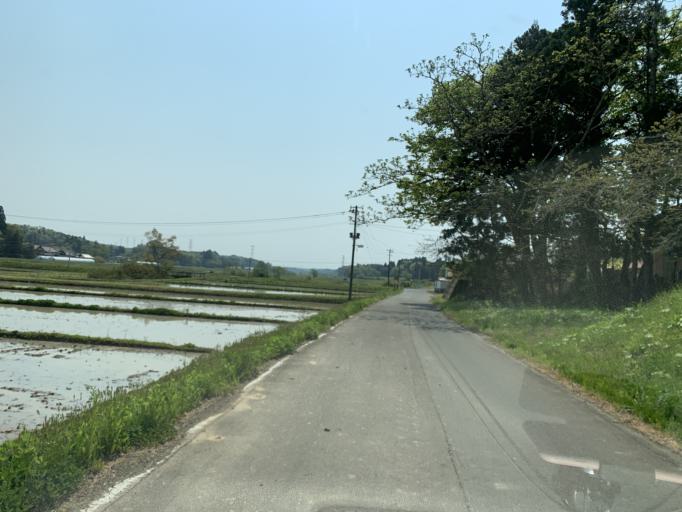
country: JP
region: Iwate
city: Ichinoseki
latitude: 38.8606
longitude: 141.0633
